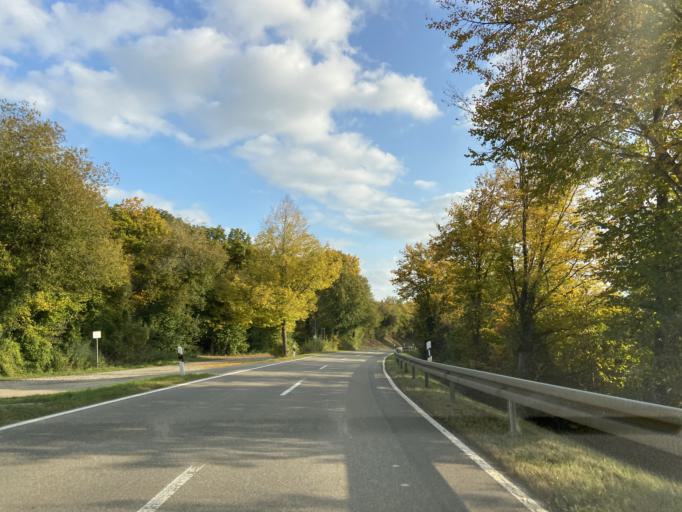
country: DE
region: Baden-Wuerttemberg
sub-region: Tuebingen Region
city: Scheer
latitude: 48.0817
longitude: 9.2926
